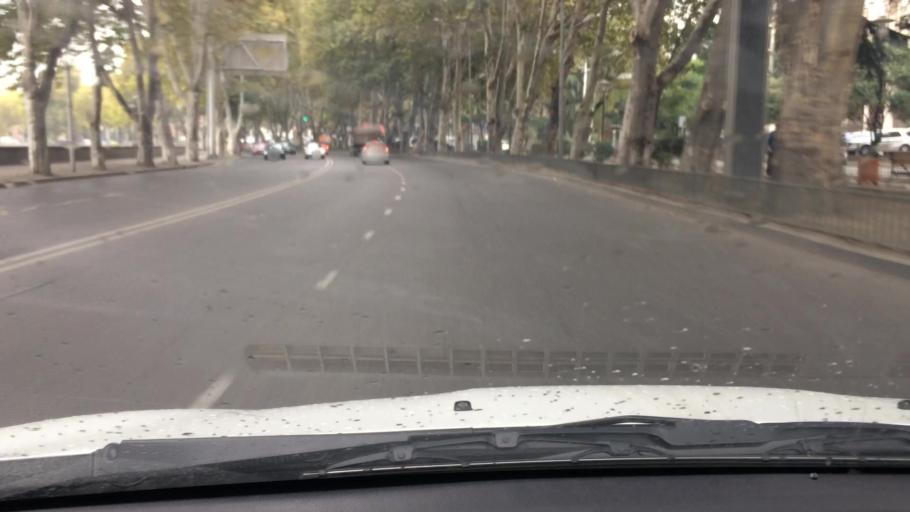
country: GE
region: T'bilisi
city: Tbilisi
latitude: 41.6991
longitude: 44.8087
